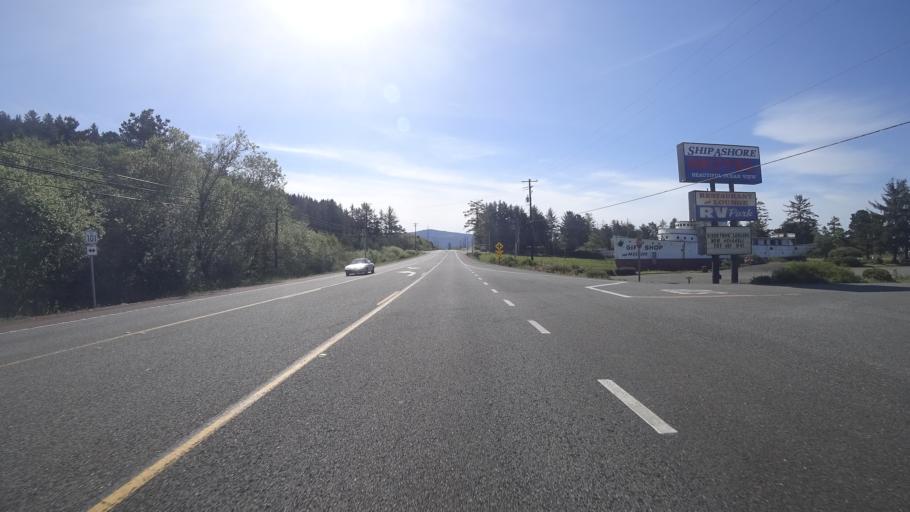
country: US
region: Oregon
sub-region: Curry County
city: Harbor
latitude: 41.9471
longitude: -124.1959
